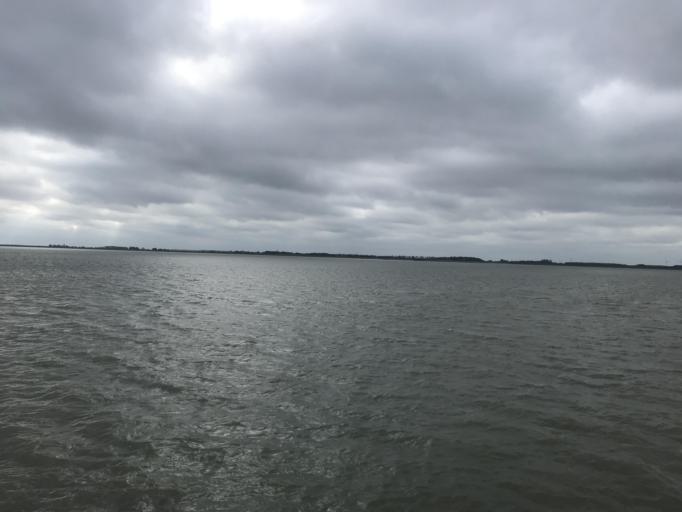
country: NL
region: Groningen
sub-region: Gemeente Delfzijl
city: Delfzijl
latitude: 53.3244
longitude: 7.0439
